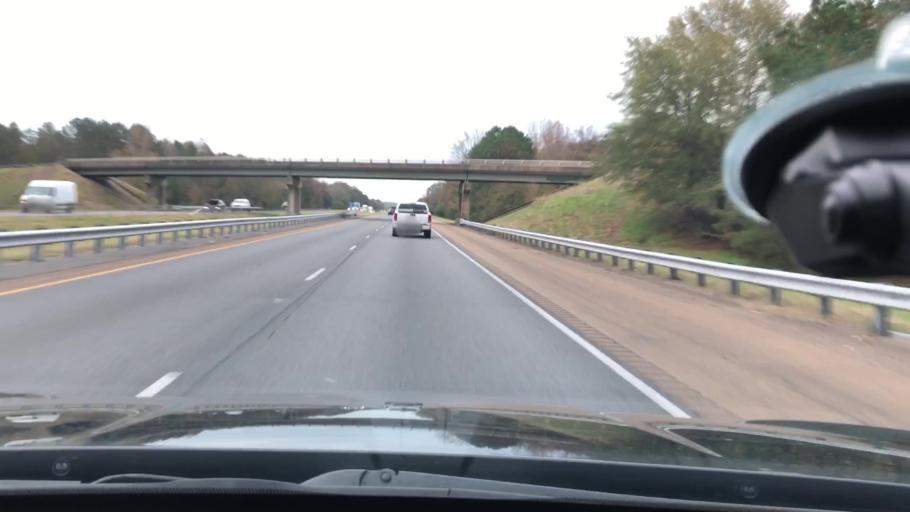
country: US
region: Arkansas
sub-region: Nevada County
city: Prescott
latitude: 33.8800
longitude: -93.3287
